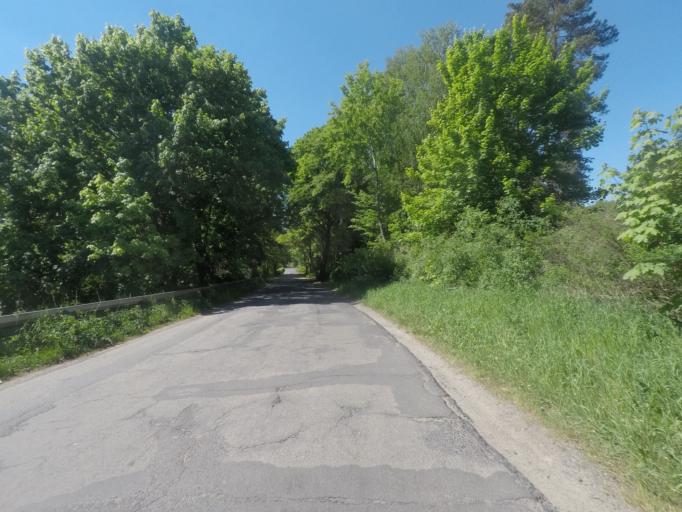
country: DE
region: Brandenburg
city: Melchow
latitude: 52.8492
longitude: 13.7153
